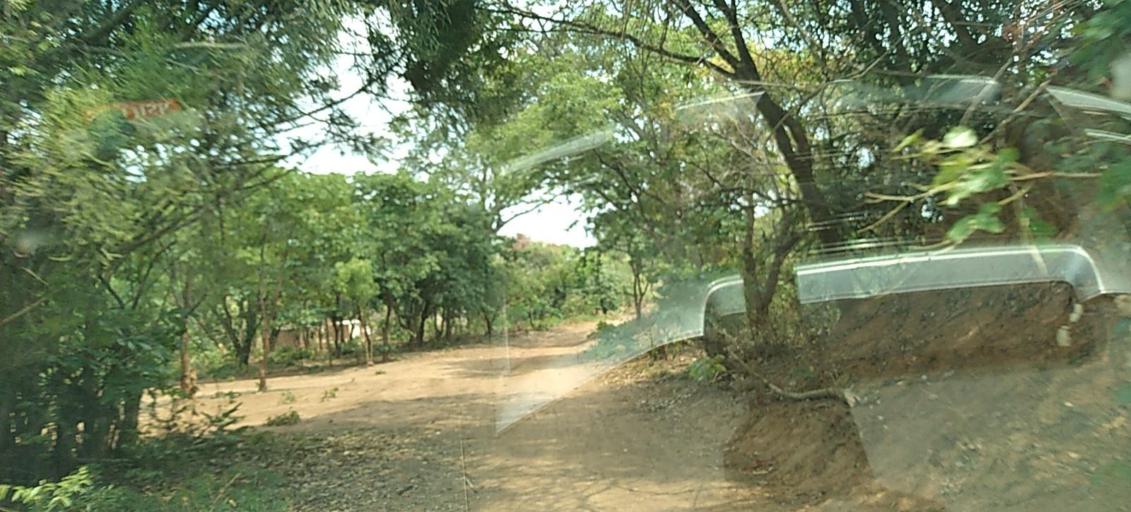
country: CD
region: Katanga
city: Kipushi
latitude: -12.0350
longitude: 27.4363
